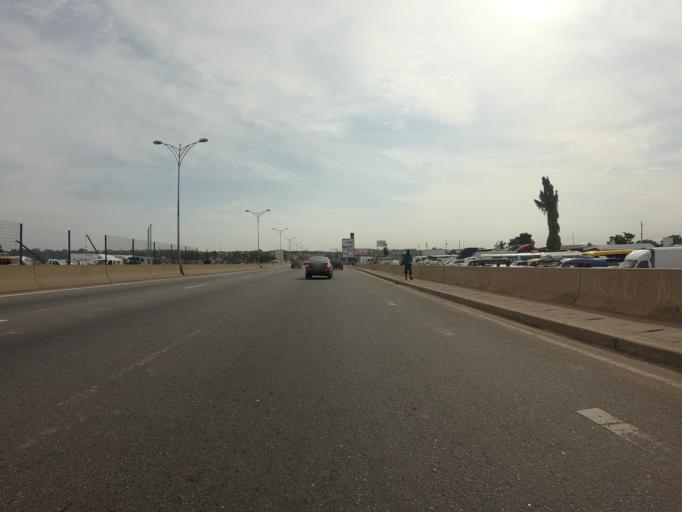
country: GH
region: Greater Accra
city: Dome
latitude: 5.6115
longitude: -0.2304
